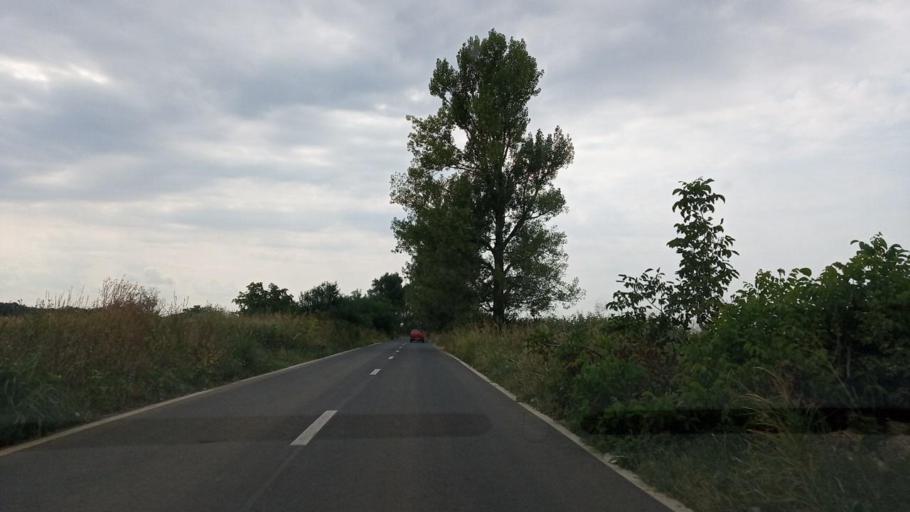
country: RO
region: Giurgiu
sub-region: Comuna Gostinari
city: Gostinari
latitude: 44.1732
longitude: 26.2313
